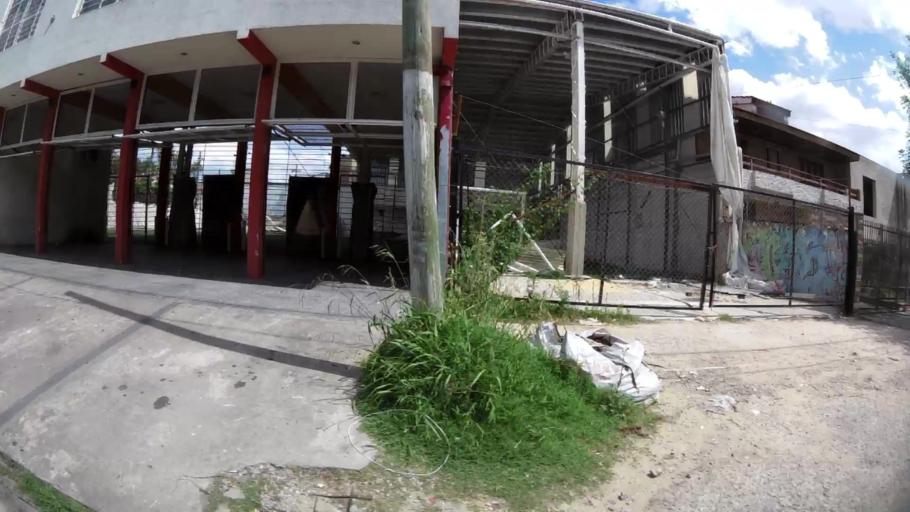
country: AR
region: Buenos Aires
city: Ituzaingo
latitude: -34.6484
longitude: -58.6617
